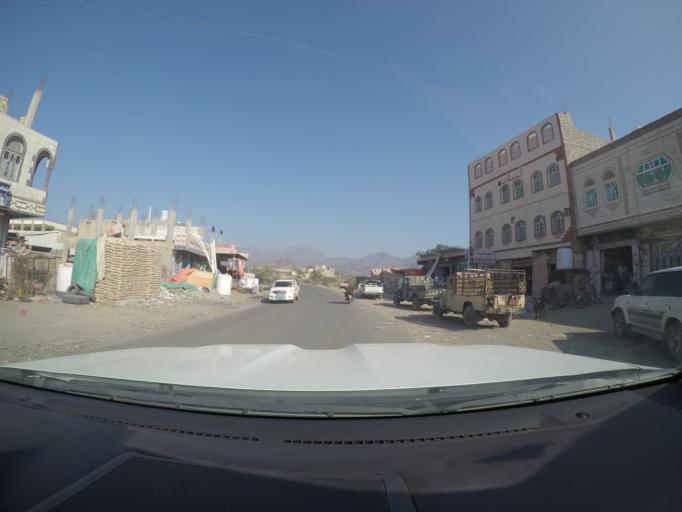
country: YE
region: Lahij
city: Habil ar Raydah
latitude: 13.6475
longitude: 44.8568
